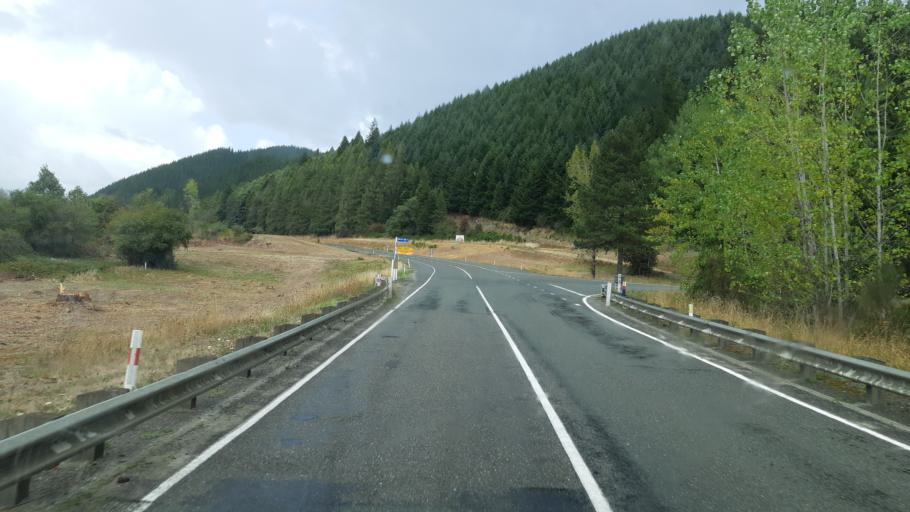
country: NZ
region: Tasman
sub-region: Tasman District
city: Wakefield
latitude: -41.4729
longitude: 172.8442
